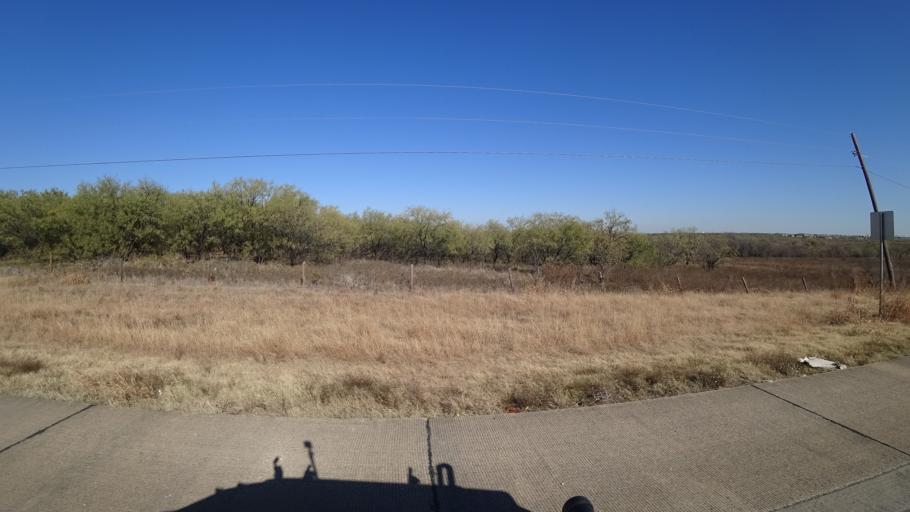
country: US
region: Texas
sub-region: Denton County
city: The Colony
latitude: 33.0498
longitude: -96.9284
